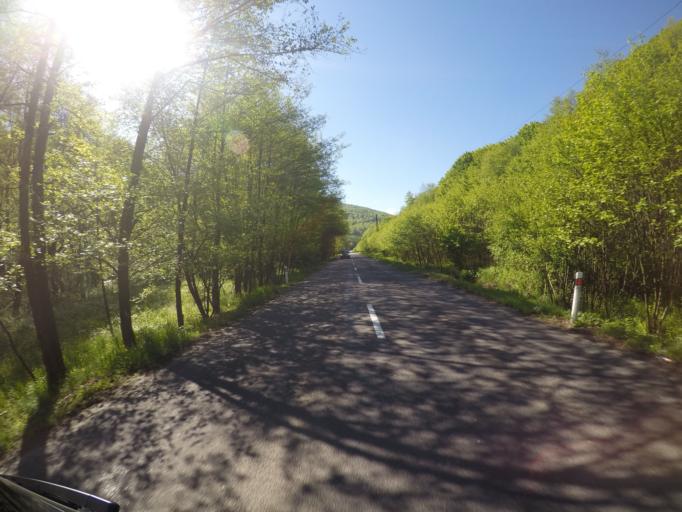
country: SK
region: Banskobystricky
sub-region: Okres Banska Bystrica
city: Banska Stiavnica
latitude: 48.5558
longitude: 19.0040
